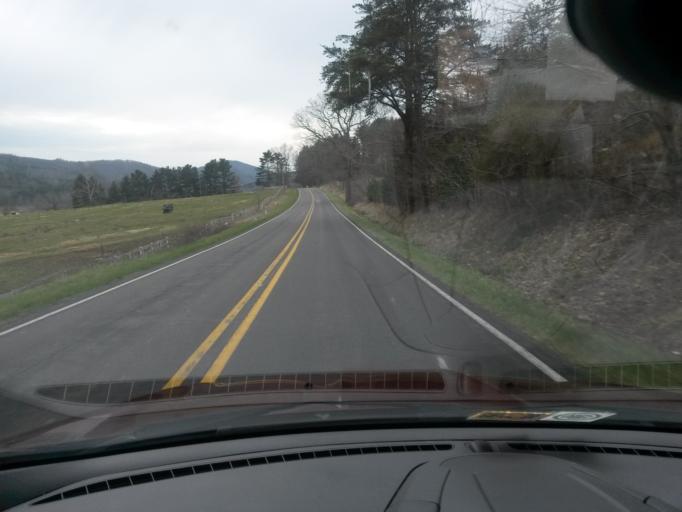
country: US
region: Virginia
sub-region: Bath County
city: Warm Springs
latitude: 38.2071
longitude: -79.7239
